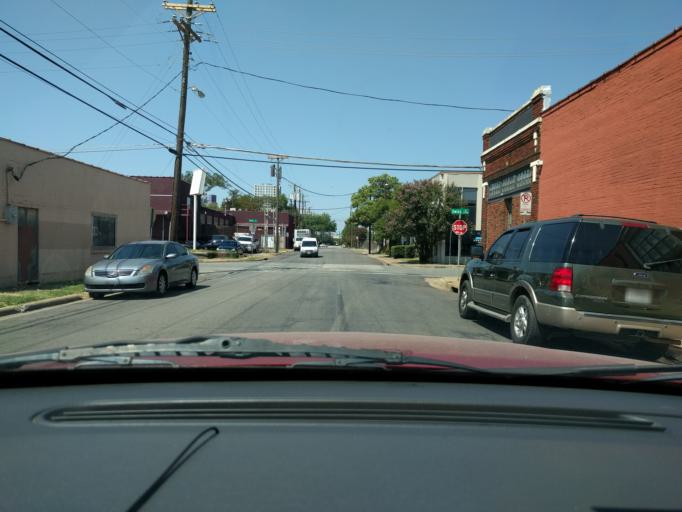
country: US
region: Texas
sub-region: Dallas County
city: Dallas
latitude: 32.7870
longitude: -96.7875
